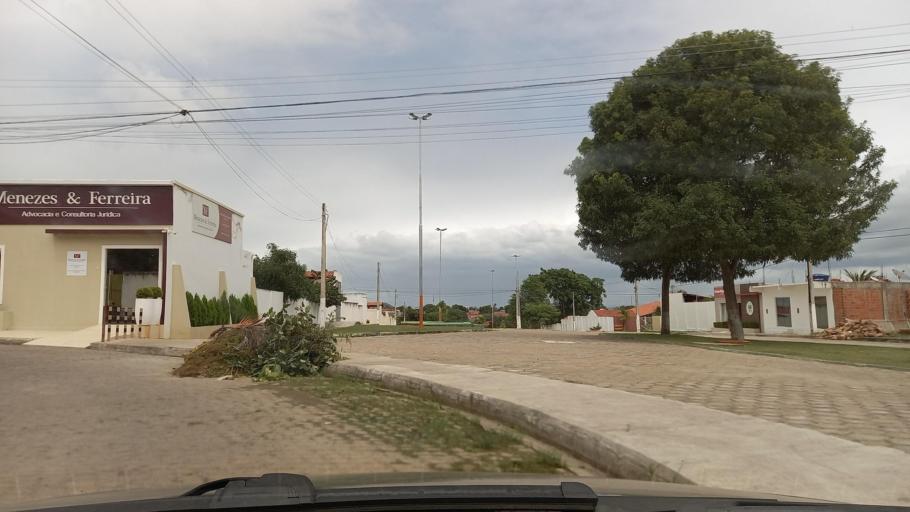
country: BR
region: Sergipe
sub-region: Caninde De Sao Francisco
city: Caninde de Sao Francisco
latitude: -9.6094
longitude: -37.7654
